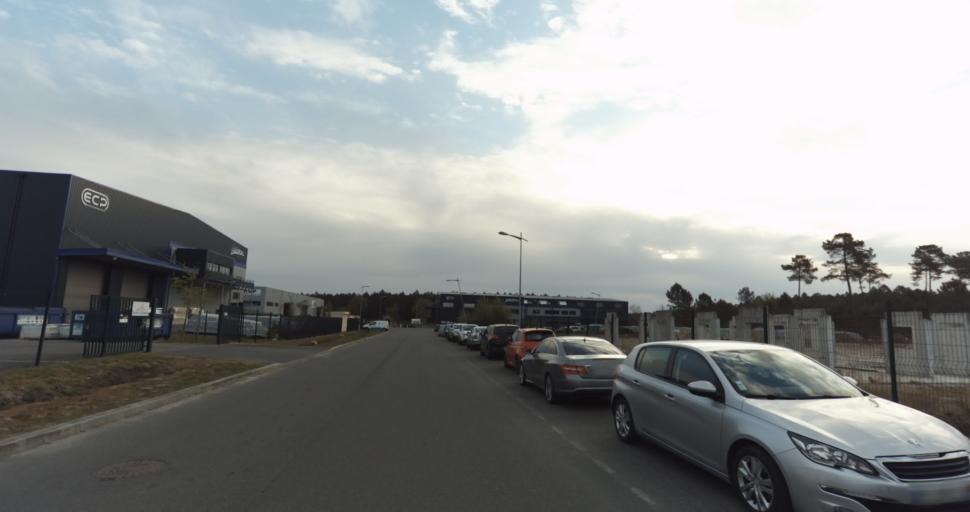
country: FR
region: Aquitaine
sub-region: Departement de la Gironde
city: Martignas-sur-Jalle
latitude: 44.7872
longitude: -0.7777
